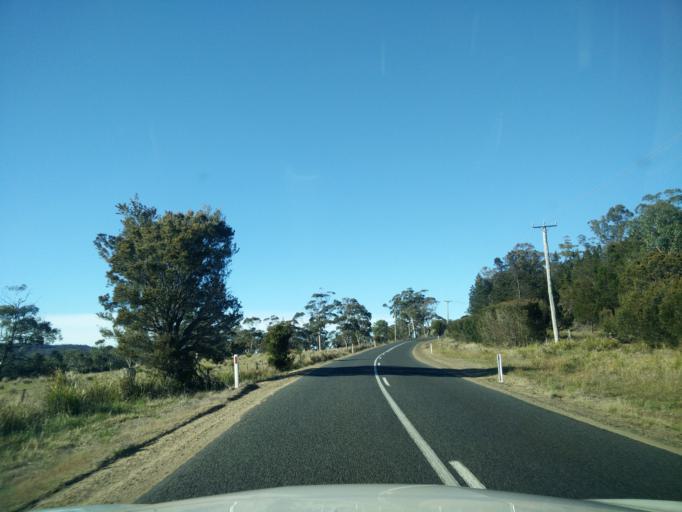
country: AU
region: Tasmania
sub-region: Break O'Day
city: St Helens
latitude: -41.9153
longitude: 148.2485
